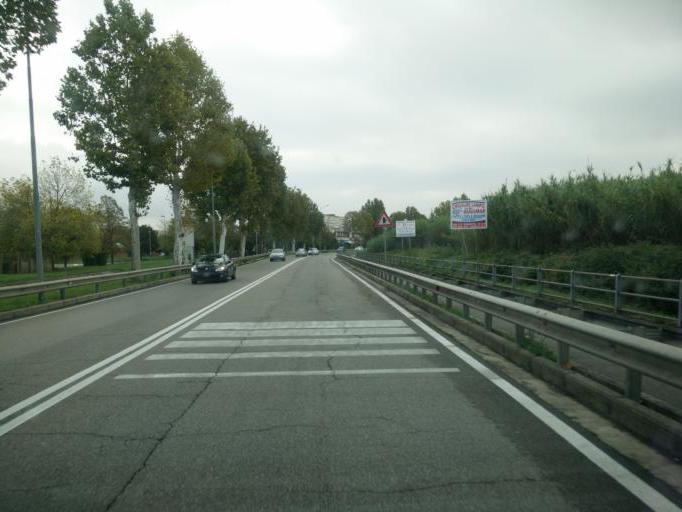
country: IT
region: Tuscany
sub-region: Province of Florence
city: San Donnino
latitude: 43.8102
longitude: 11.1677
